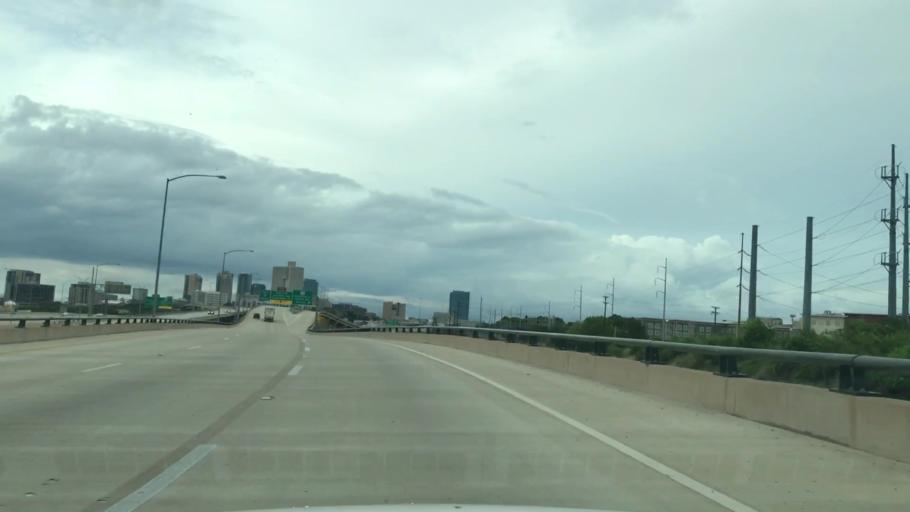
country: US
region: Texas
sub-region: Tarrant County
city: Fort Worth
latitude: 32.7348
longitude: -97.3553
